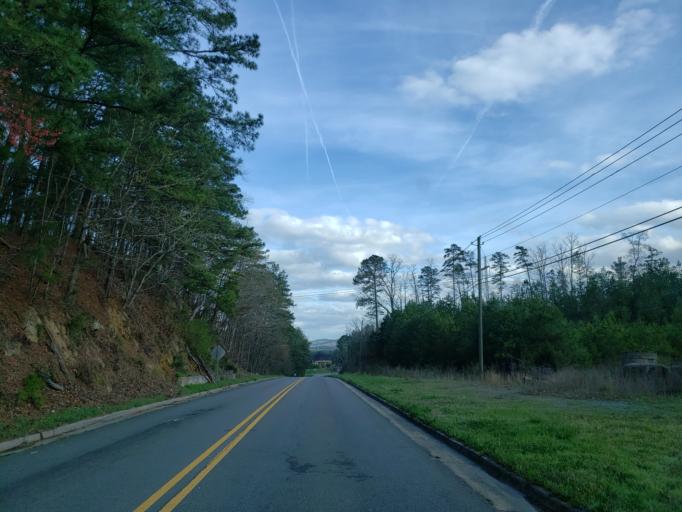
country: US
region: Georgia
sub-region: Bartow County
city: Cartersville
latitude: 34.2404
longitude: -84.8089
